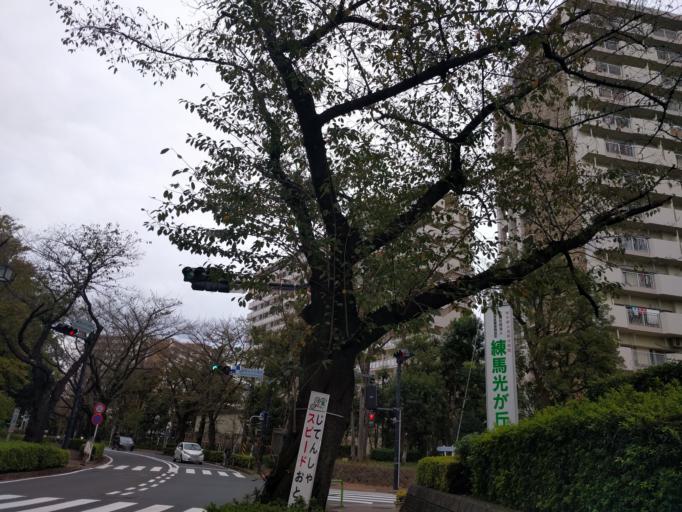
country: JP
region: Saitama
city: Wako
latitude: 35.7624
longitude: 139.6301
